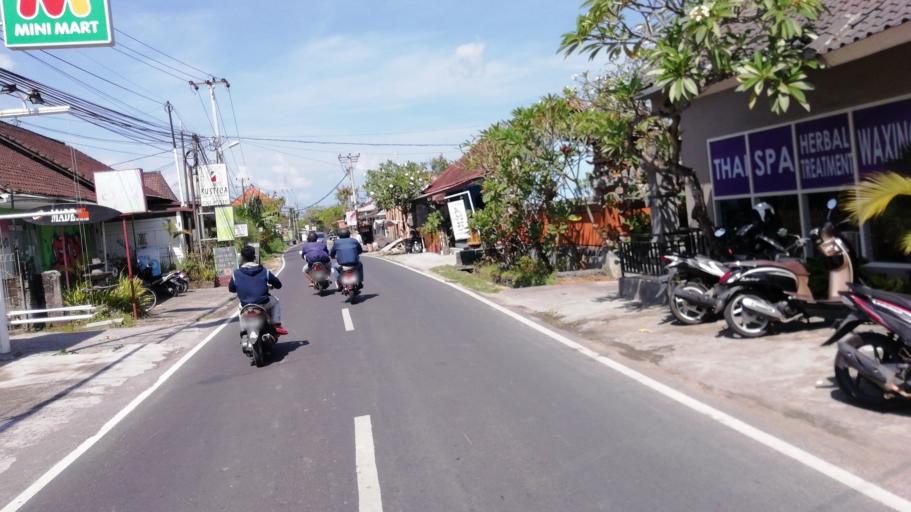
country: ID
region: Bali
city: Banjar Gunungpande
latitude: -8.6448
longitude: 115.1415
